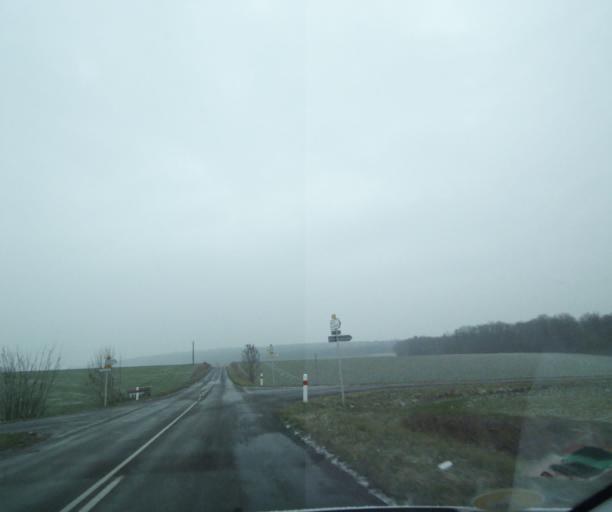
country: FR
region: Champagne-Ardenne
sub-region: Departement de la Haute-Marne
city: Wassy
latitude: 48.4811
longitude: 4.9995
